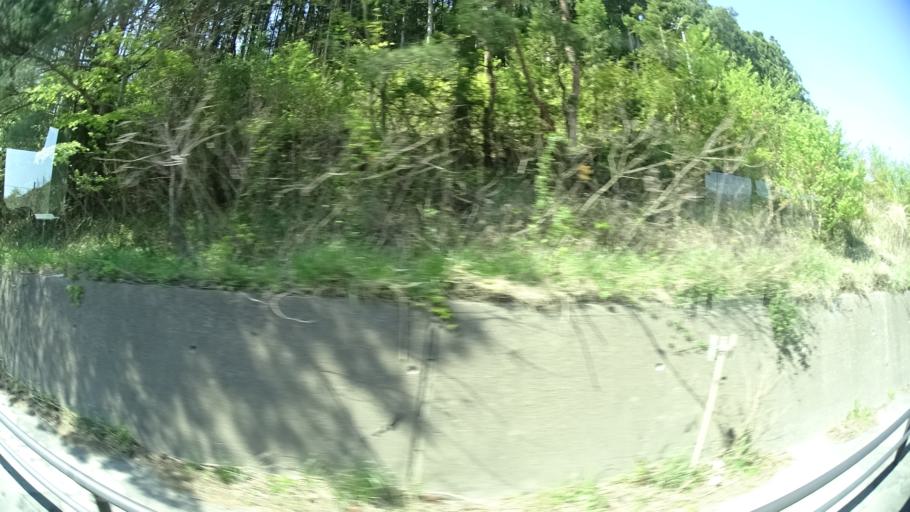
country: JP
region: Iwate
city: Ofunato
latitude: 38.9798
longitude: 141.6221
